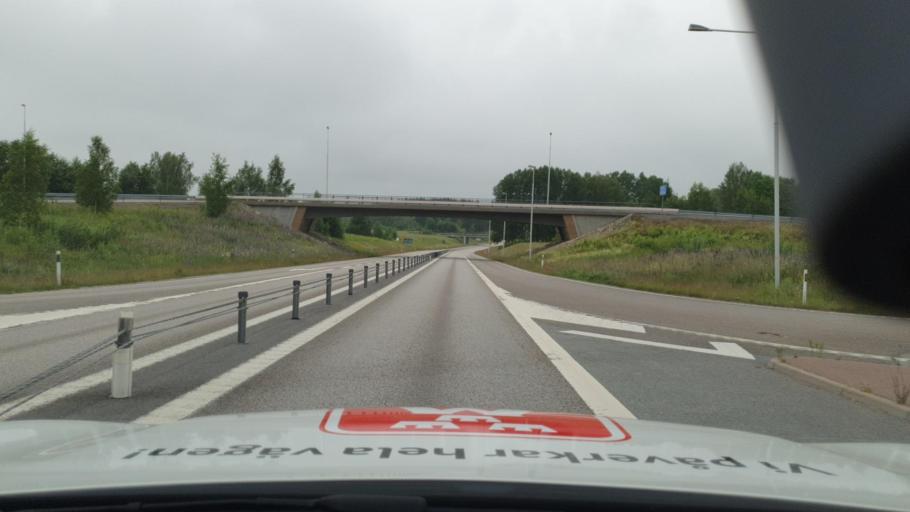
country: SE
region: Vaermland
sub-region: Karlstads Kommun
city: Edsvalla
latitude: 59.5169
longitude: 13.2147
